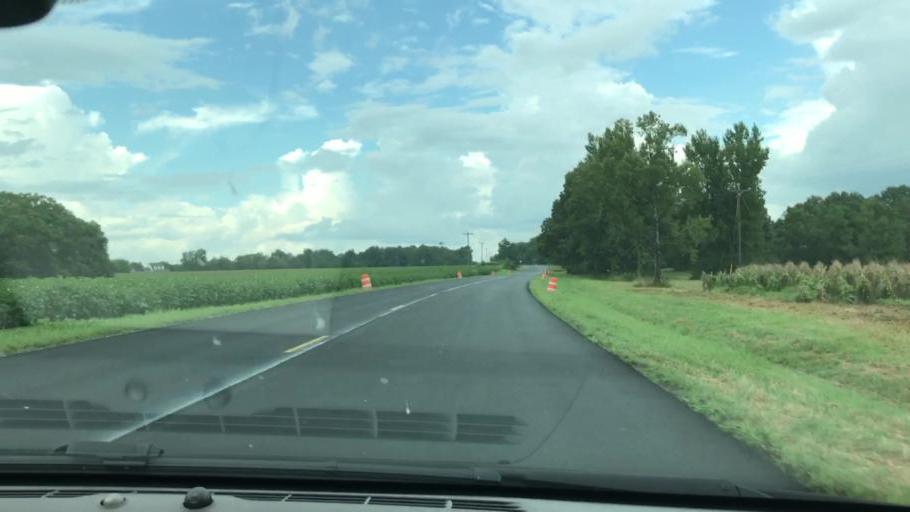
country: US
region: Georgia
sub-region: Early County
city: Blakely
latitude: 31.4308
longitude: -84.9710
